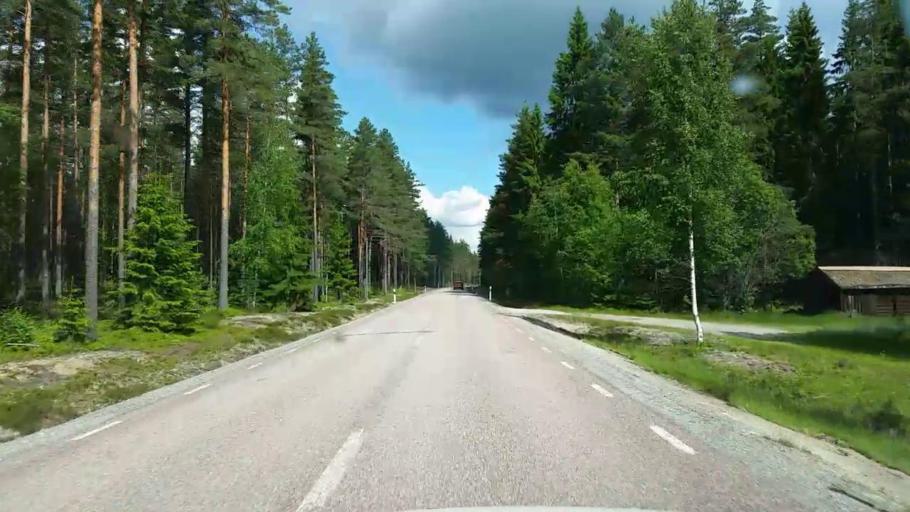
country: SE
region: Vaestmanland
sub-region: Skinnskattebergs Kommun
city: Skinnskatteberg
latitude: 59.8112
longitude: 15.8407
